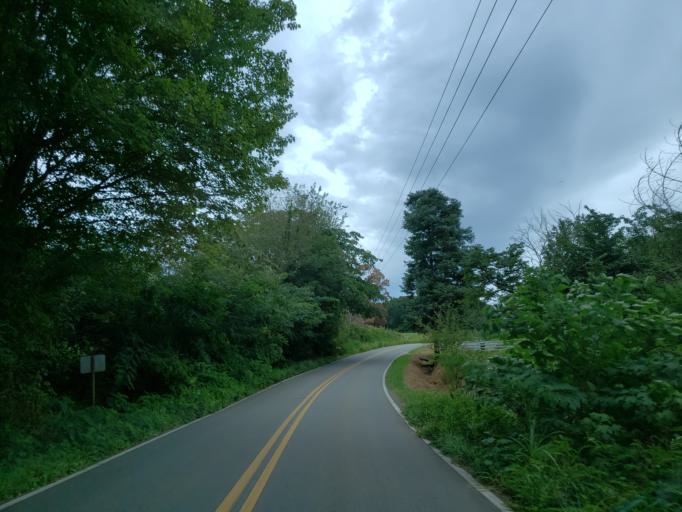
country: US
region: Georgia
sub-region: Pickens County
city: Jasper
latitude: 34.4150
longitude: -84.5669
